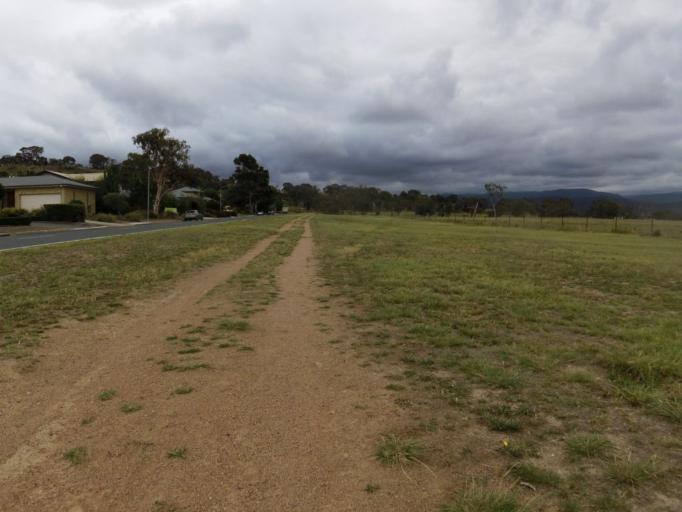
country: AU
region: Australian Capital Territory
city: Macquarie
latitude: -35.3475
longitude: 149.0262
